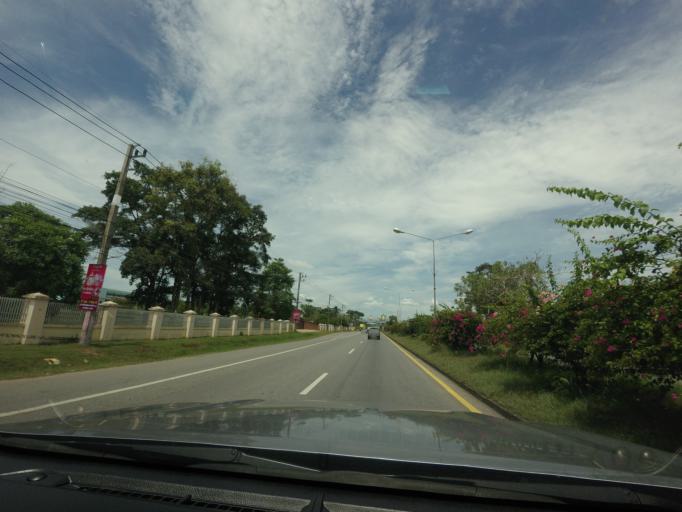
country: TH
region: Songkhla
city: Singhanakhon
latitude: 7.2410
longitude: 100.5475
